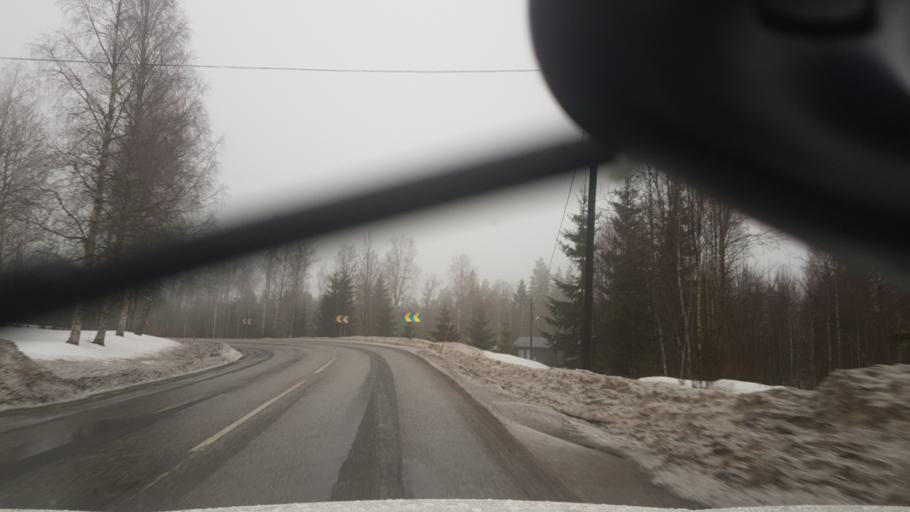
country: SE
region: Vaermland
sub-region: Eda Kommun
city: Amotfors
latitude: 59.5803
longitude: 12.2590
